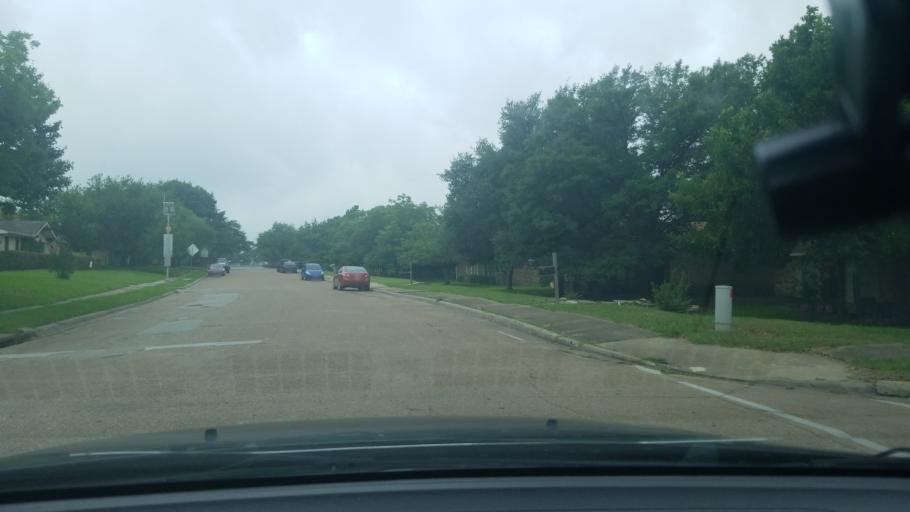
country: US
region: Texas
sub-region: Dallas County
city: Mesquite
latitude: 32.7833
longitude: -96.6388
